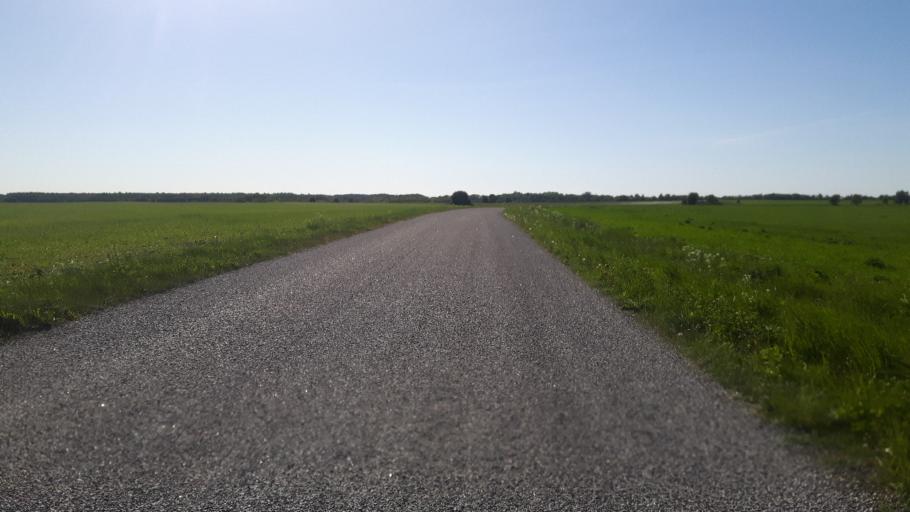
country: EE
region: Ida-Virumaa
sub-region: Kohtla-Jaerve linn
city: Kohtla-Jarve
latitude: 59.4305
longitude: 27.2193
